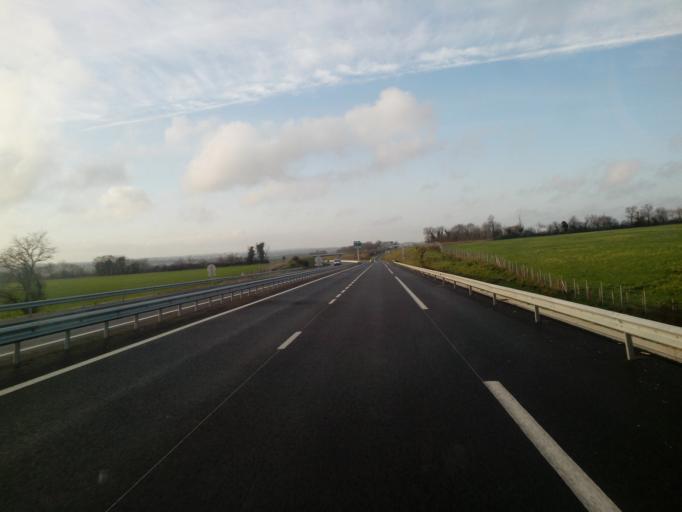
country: FR
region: Poitou-Charentes
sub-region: Departement des Deux-Sevres
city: Le Pin
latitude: 46.8955
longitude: -0.6232
